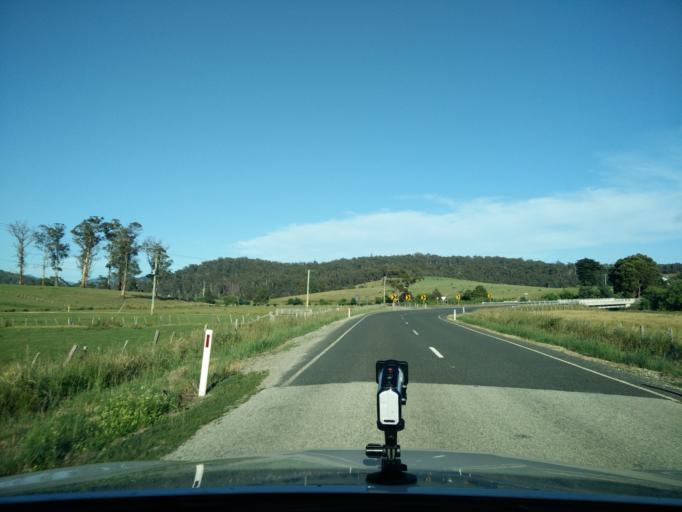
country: AU
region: Tasmania
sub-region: Break O'Day
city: St Helens
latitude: -41.2722
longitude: 148.1000
